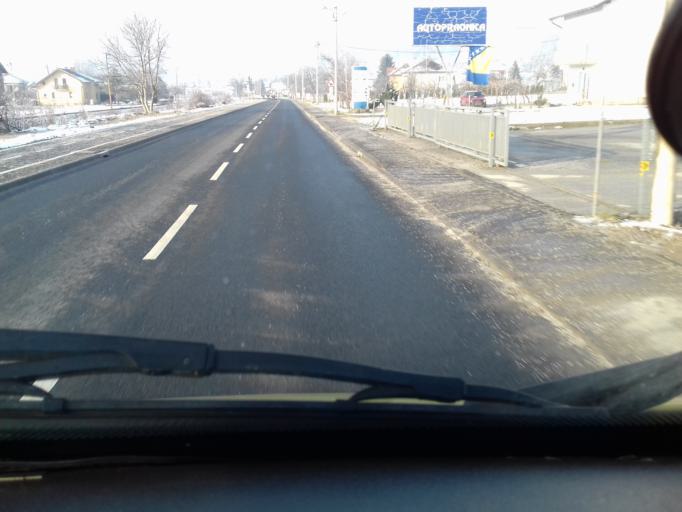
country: BA
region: Federation of Bosnia and Herzegovina
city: Mahala
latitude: 43.9809
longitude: 18.2400
